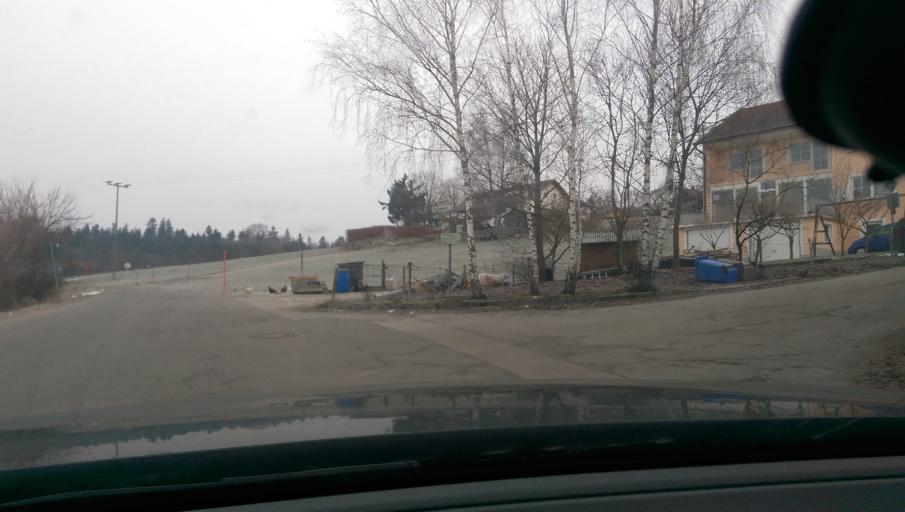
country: DE
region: Bavaria
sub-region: Lower Bavaria
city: Hutthurm
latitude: 48.6620
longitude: 13.4822
